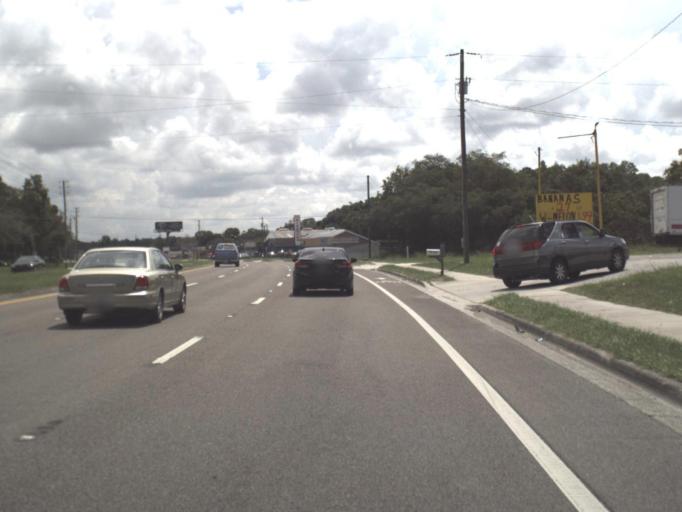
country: US
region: Florida
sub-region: Pasco County
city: Bayonet Point
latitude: 28.3313
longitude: -82.6354
